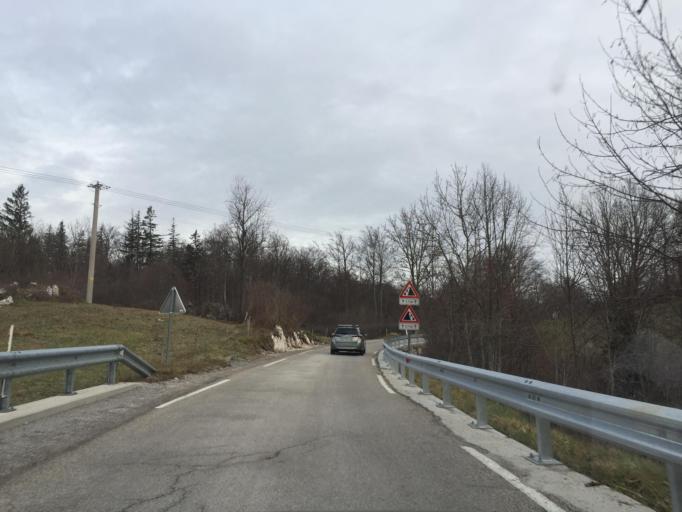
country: SI
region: Nova Gorica
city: Sempas
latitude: 45.9764
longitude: 13.7440
